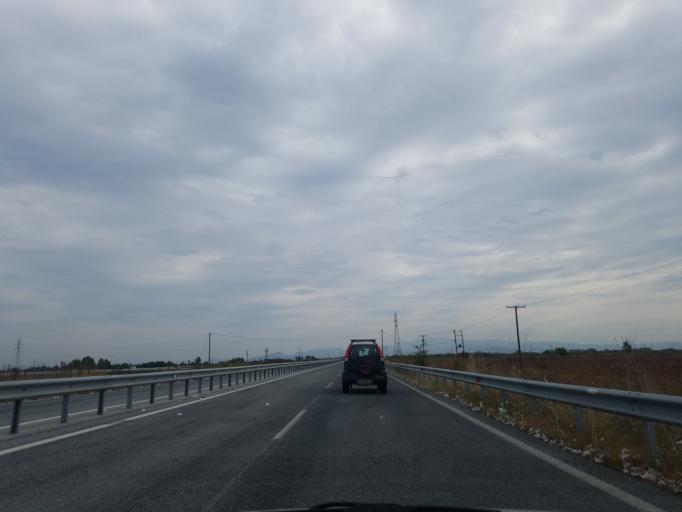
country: GR
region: Thessaly
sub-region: Nomos Kardhitsas
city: Sofades
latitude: 39.2988
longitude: 22.1432
